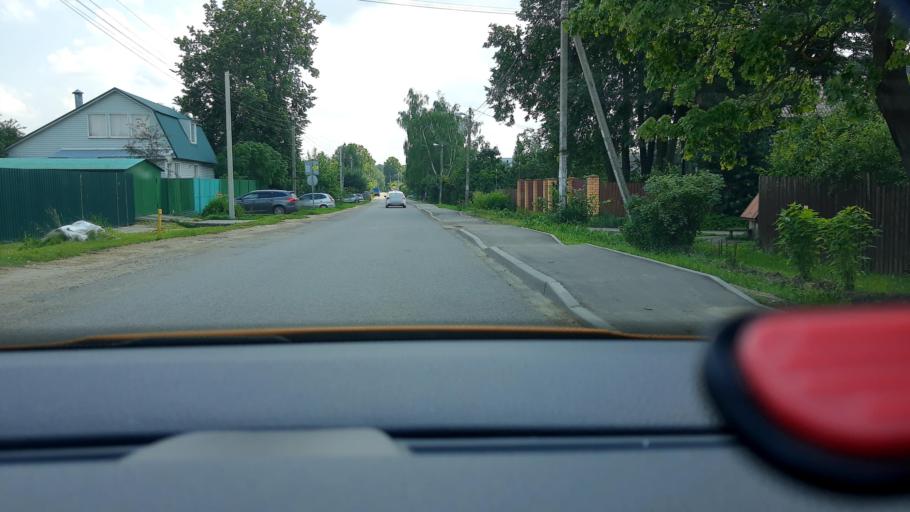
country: RU
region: Moskovskaya
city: Povedniki
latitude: 56.0043
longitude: 37.5881
